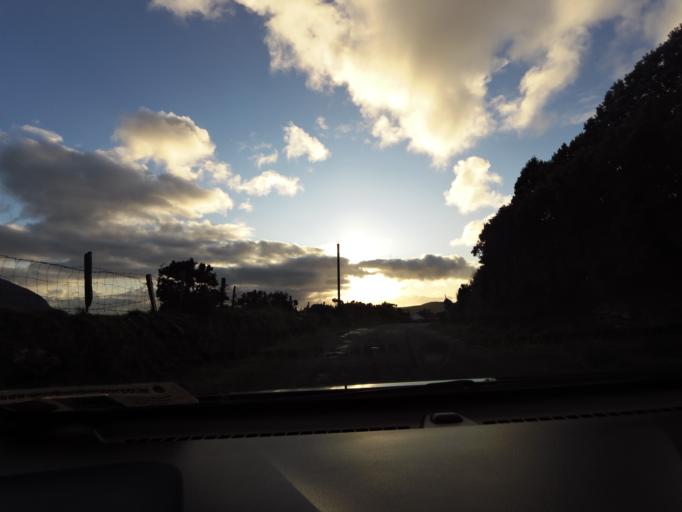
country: IE
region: Connaught
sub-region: Maigh Eo
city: Belmullet
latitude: 54.0002
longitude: -10.0329
